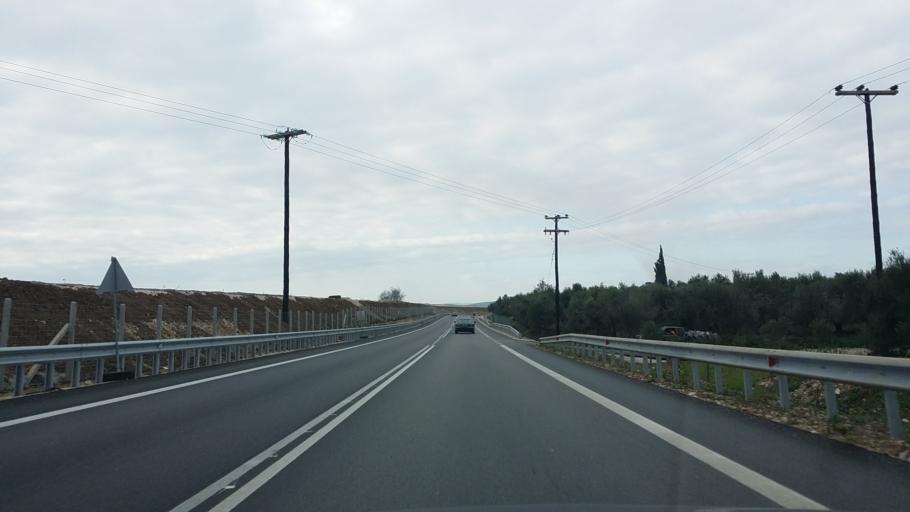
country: GR
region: West Greece
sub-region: Nomos Aitolias kai Akarnanias
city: Mesolongi
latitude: 38.3990
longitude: 21.4120
